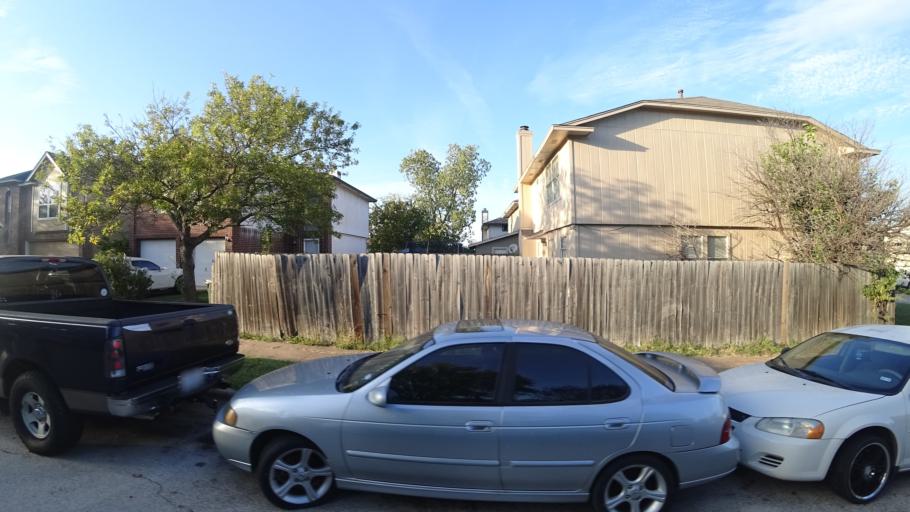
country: US
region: Texas
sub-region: Travis County
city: Pflugerville
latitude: 30.4171
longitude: -97.6478
